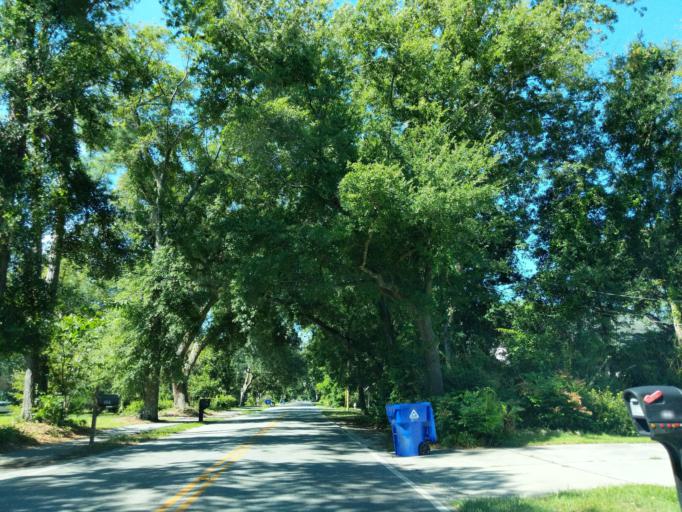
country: US
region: South Carolina
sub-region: Charleston County
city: Charleston
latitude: 32.7446
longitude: -79.9112
